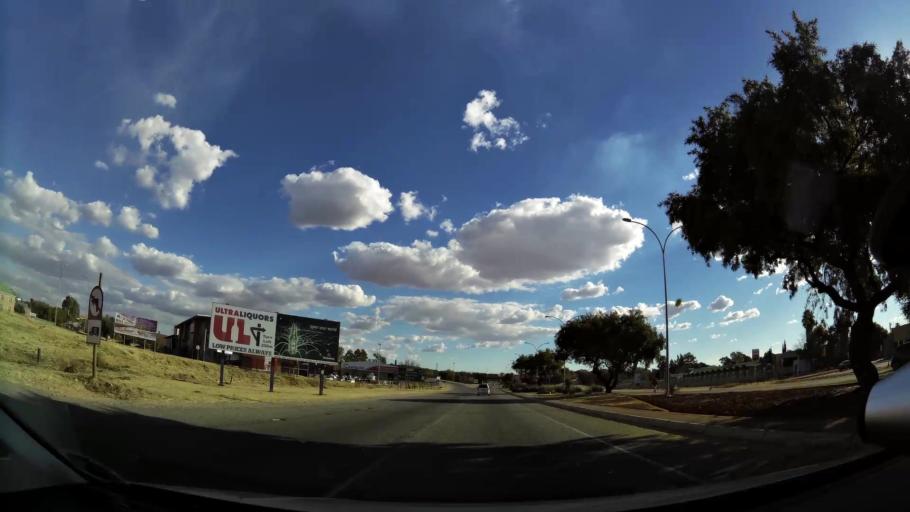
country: ZA
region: North-West
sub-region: Dr Kenneth Kaunda District Municipality
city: Klerksdorp
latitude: -26.8585
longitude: 26.6710
